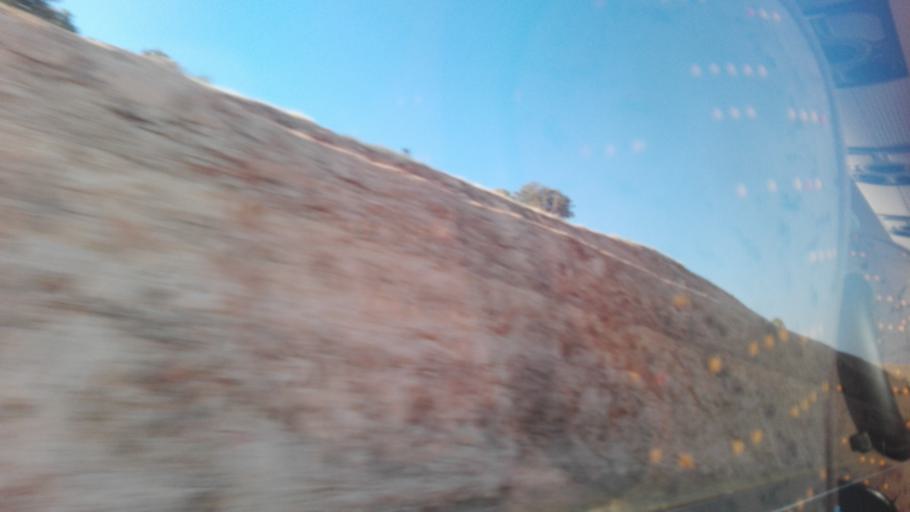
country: TR
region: Mardin
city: Ortaca
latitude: 37.5239
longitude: 41.5920
